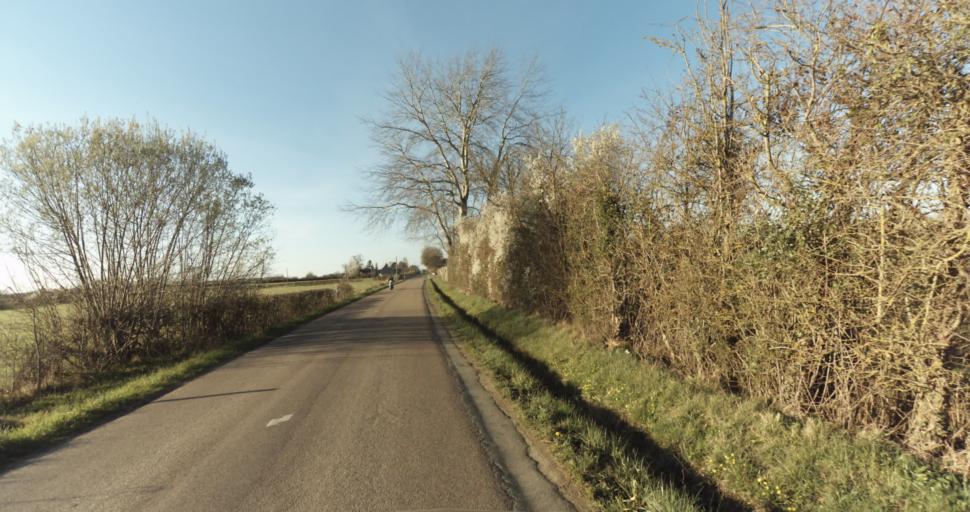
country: FR
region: Lower Normandy
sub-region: Departement du Calvados
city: Saint-Pierre-sur-Dives
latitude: 48.9670
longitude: -0.0047
